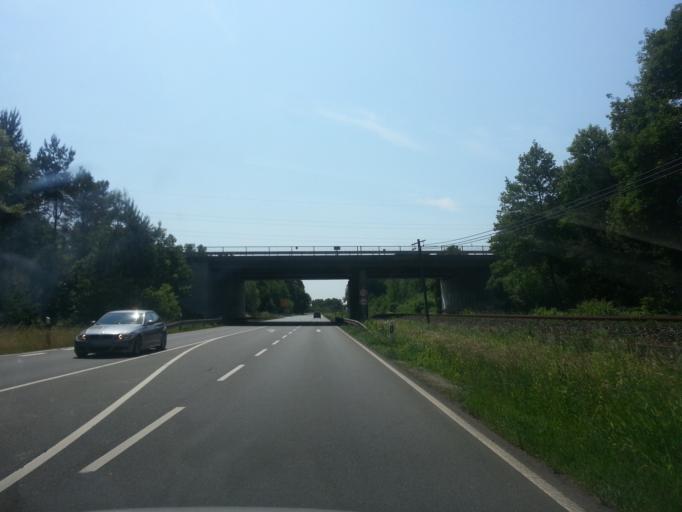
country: DE
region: Hesse
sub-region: Regierungsbezirk Darmstadt
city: Eppertshausen
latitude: 49.9566
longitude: 8.8373
